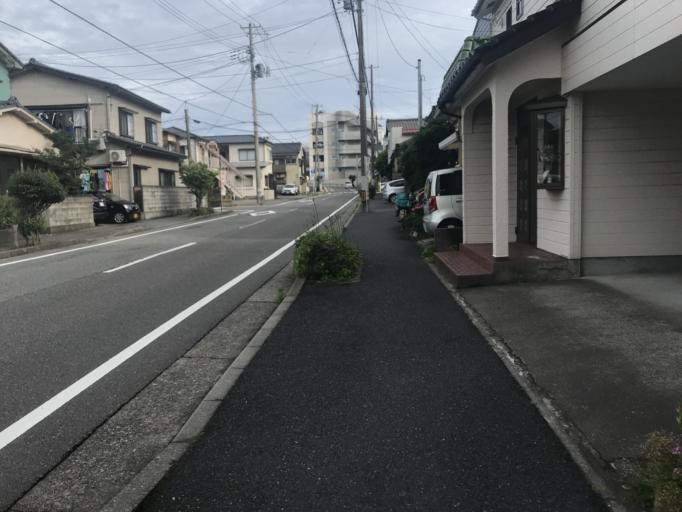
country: JP
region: Niigata
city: Niigata-shi
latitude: 37.9336
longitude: 139.0499
